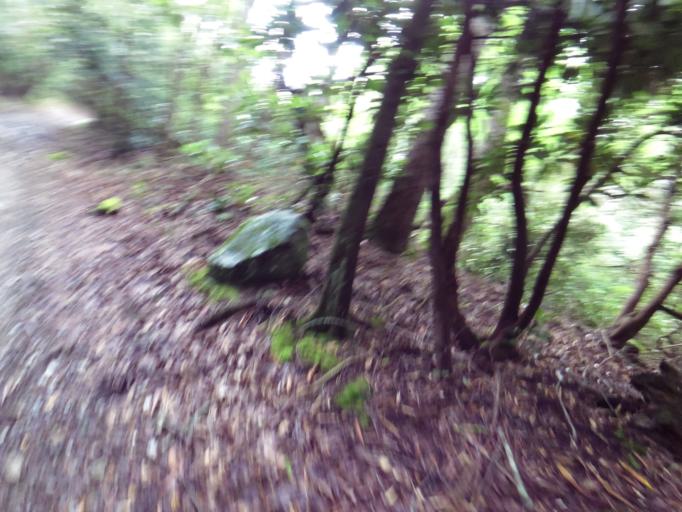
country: US
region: Tennessee
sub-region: Blount County
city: Wildwood
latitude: 35.5951
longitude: -83.7631
